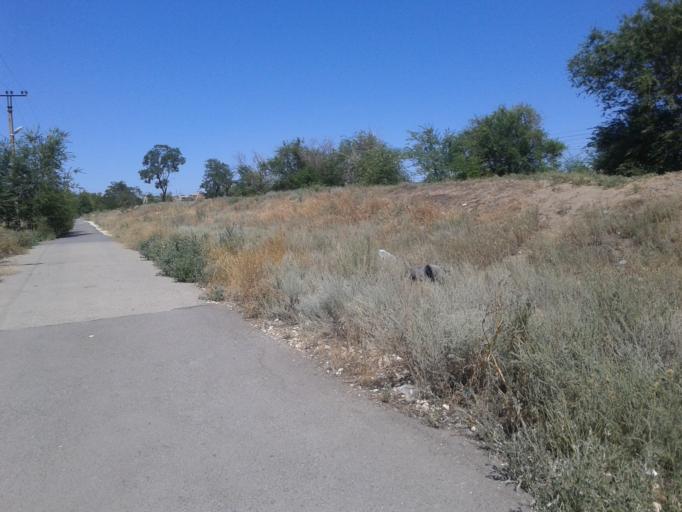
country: RU
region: Volgograd
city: Volgograd
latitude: 48.6905
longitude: 44.4461
